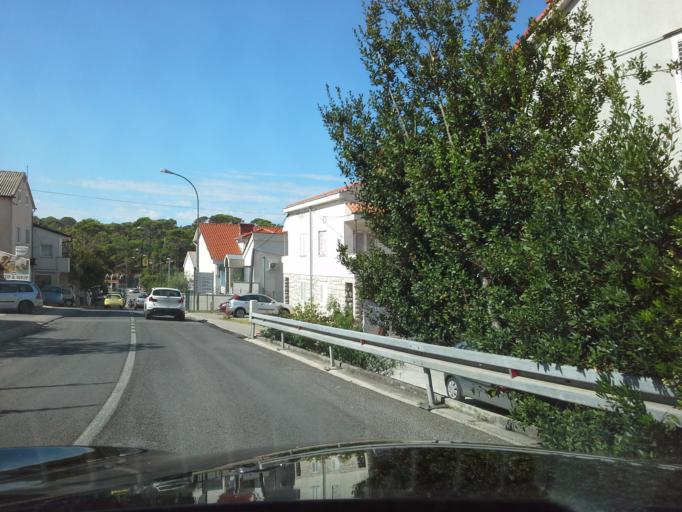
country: HR
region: Primorsko-Goranska
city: Banjol
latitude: 44.7615
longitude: 14.7625
